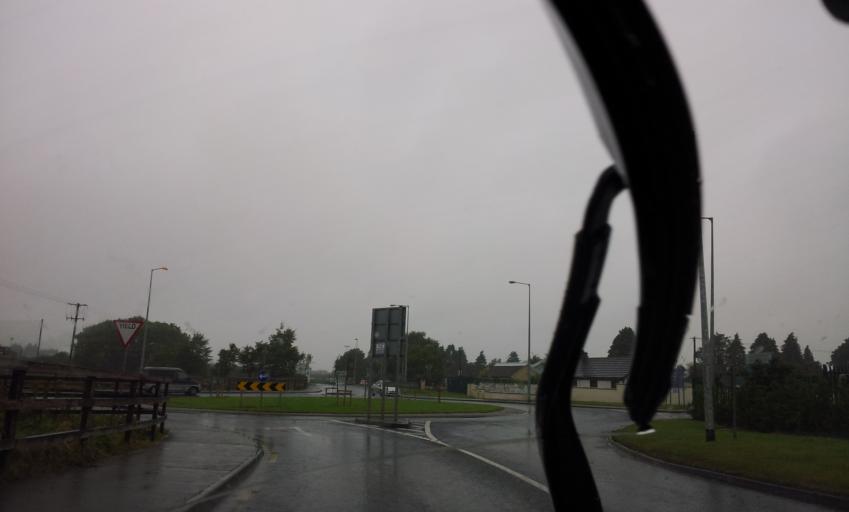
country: IE
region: Munster
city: Cashel
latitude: 52.5101
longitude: -7.8741
